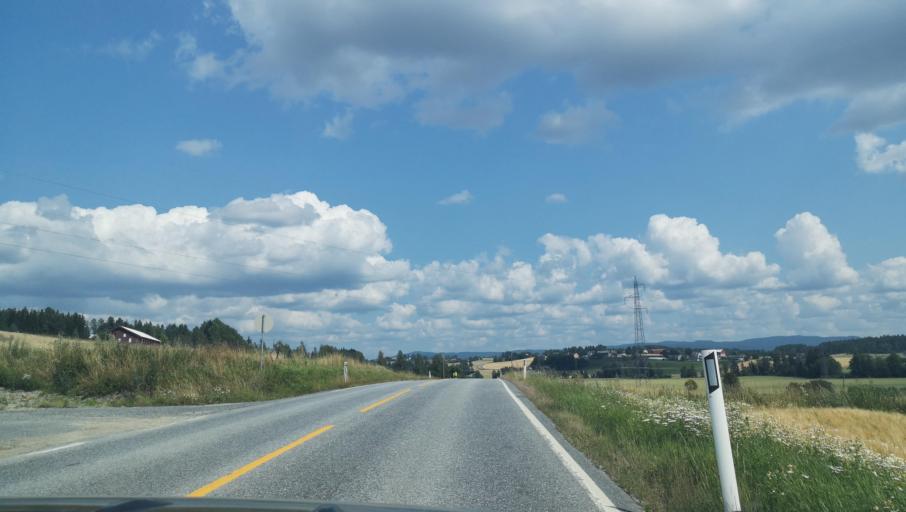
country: NO
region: Buskerud
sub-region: Ovre Eiker
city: Hokksund
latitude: 59.7172
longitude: 9.8227
